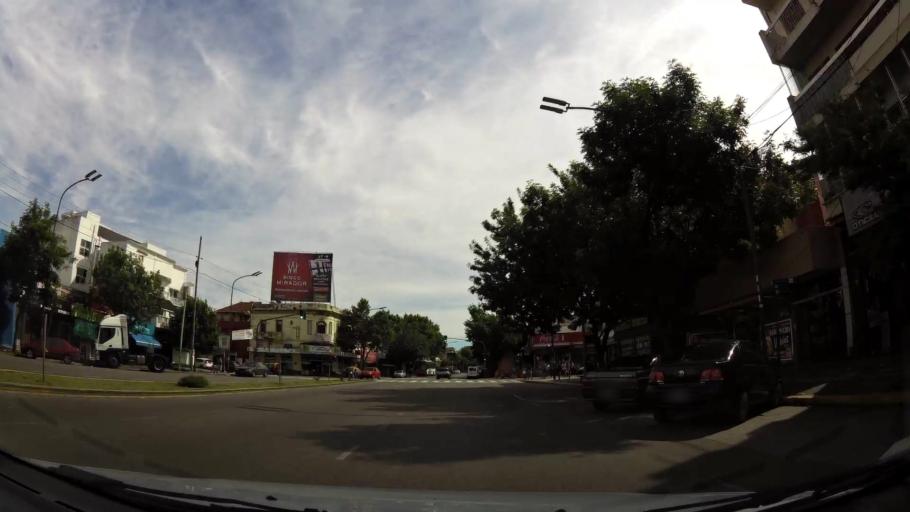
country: AR
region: Buenos Aires F.D.
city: Villa Lugano
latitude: -34.6533
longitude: -58.5044
